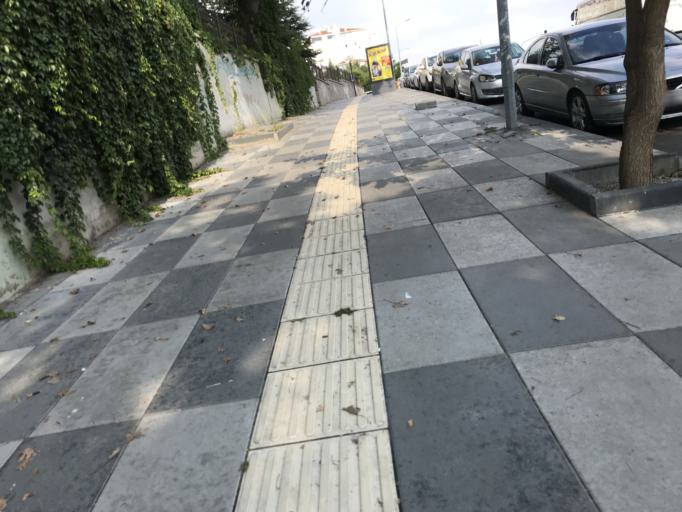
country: TR
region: Ankara
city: Ankara
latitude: 39.9176
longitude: 32.8231
